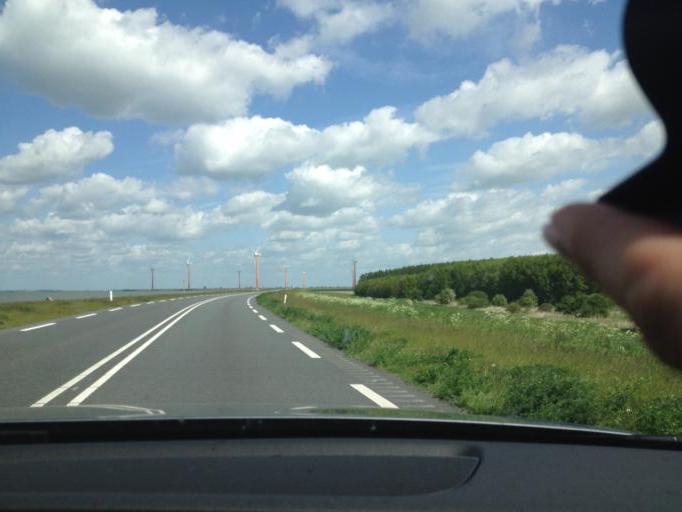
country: NL
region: North Holland
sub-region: Gemeente Naarden
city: Naarden
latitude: 52.3577
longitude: 5.1331
